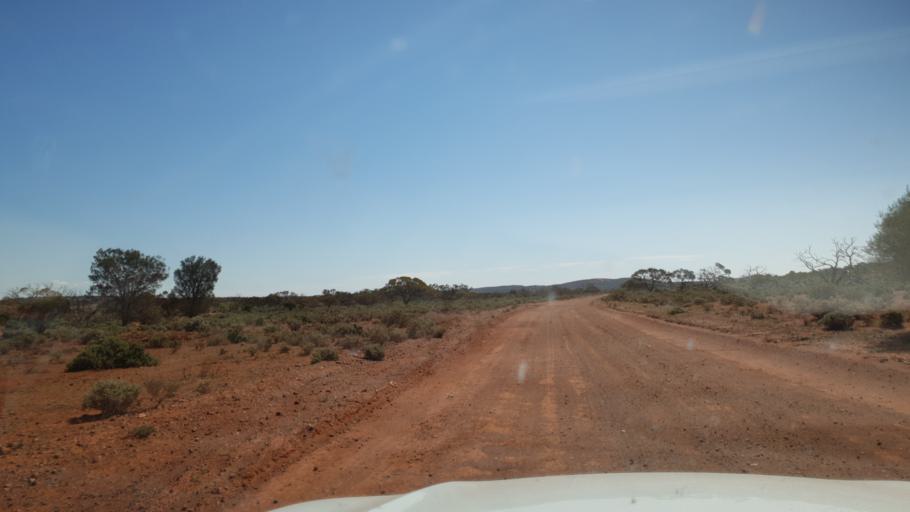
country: AU
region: South Australia
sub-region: Kimba
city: Caralue
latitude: -32.5422
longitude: 136.5261
